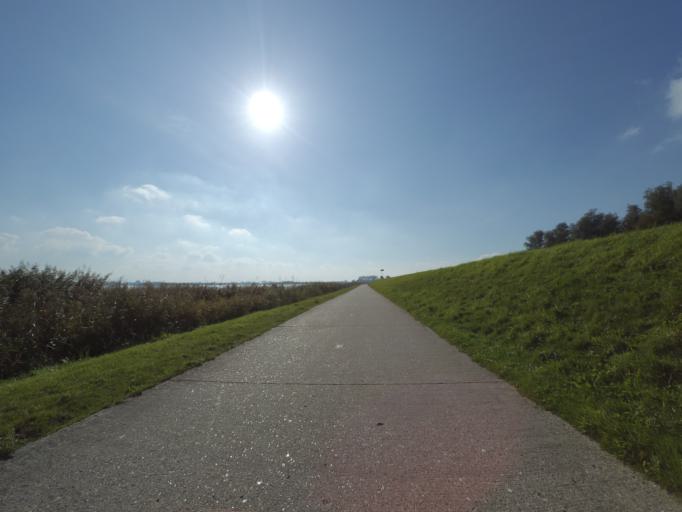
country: NL
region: Gelderland
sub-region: Gemeente Harderwijk
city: Harderwijk
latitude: 52.3758
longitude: 5.6202
